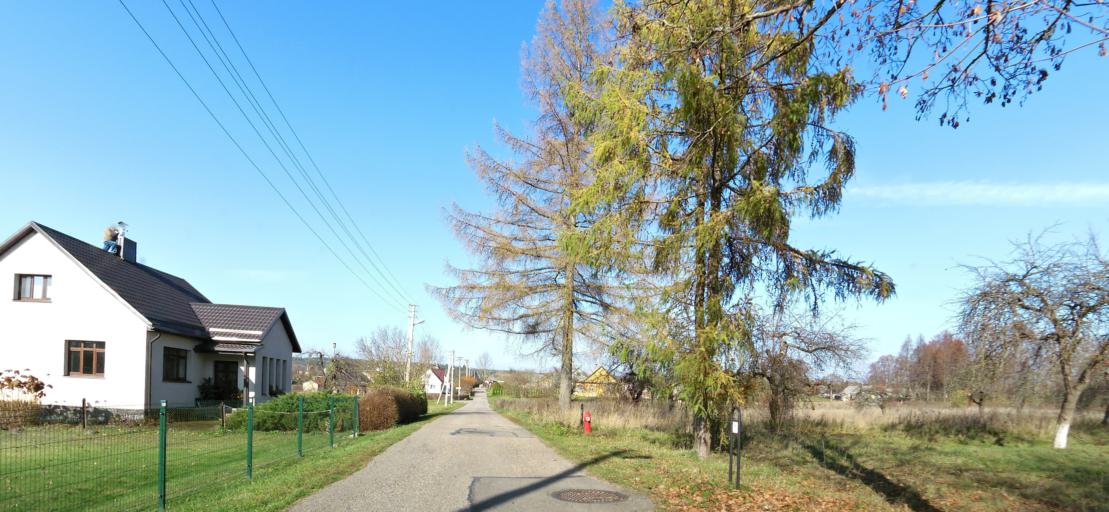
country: LT
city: Aukstadvaris
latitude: 54.5777
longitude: 24.5194
